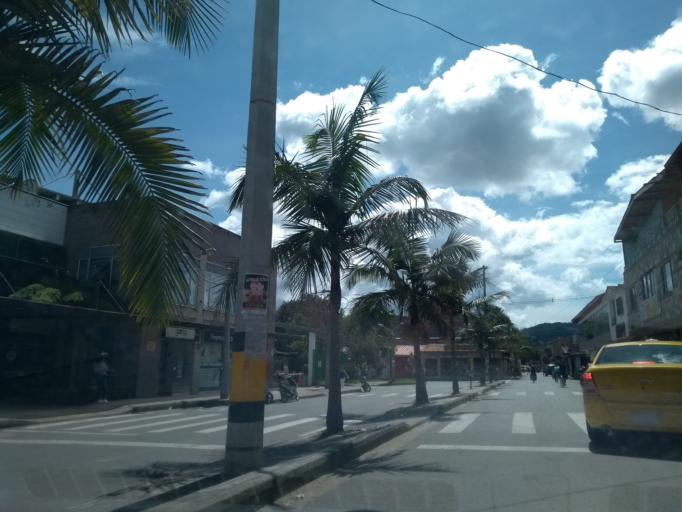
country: CO
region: Antioquia
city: La Ceja
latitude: 6.0317
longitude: -75.4283
